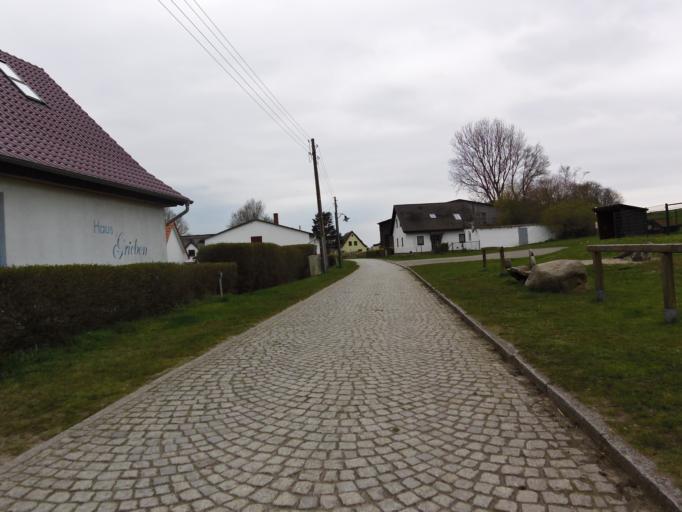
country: DE
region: Mecklenburg-Vorpommern
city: Hiddensee
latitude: 54.5927
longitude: 13.1287
